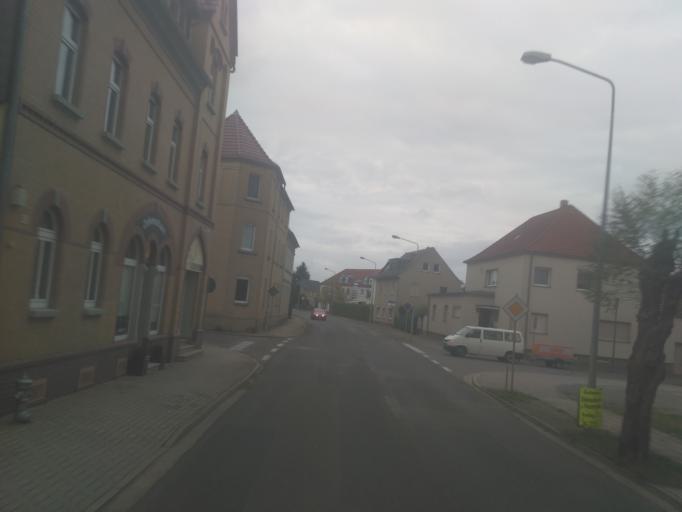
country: DE
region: Brandenburg
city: Elsterwerda
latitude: 51.4609
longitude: 13.5258
